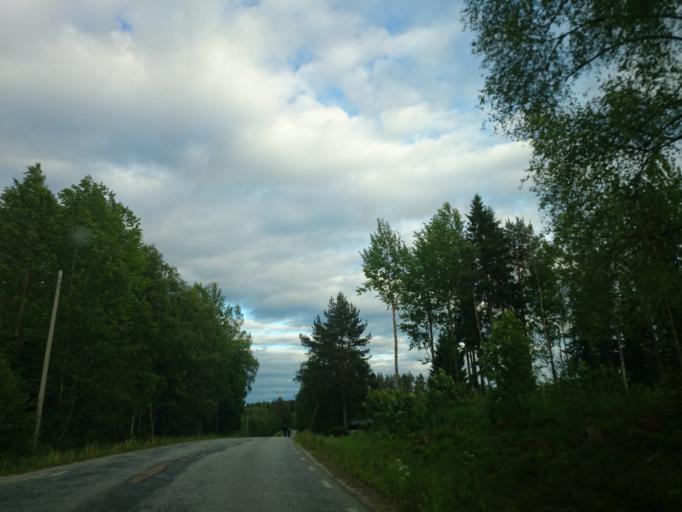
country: SE
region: Vaesternorrland
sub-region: Haernoesands Kommun
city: Haernoesand
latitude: 62.5789
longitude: 17.8199
